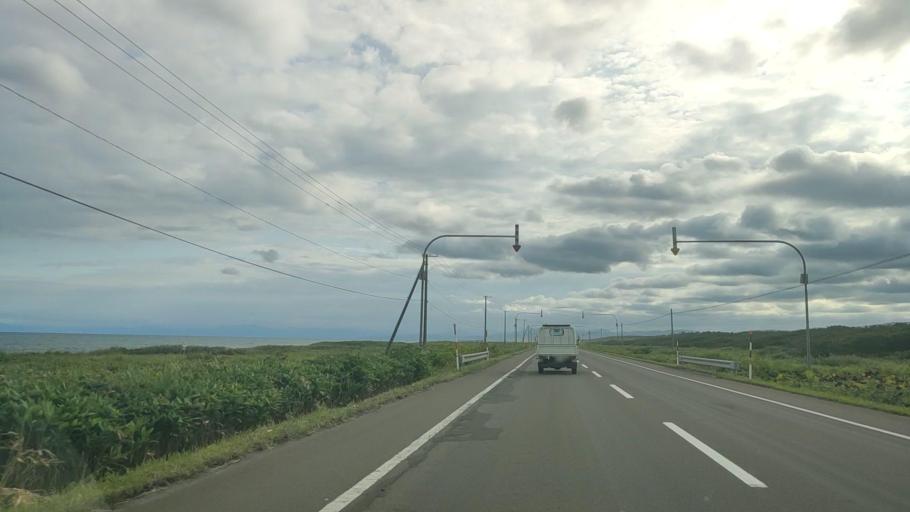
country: JP
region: Hokkaido
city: Niseko Town
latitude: 42.5718
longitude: 140.4454
